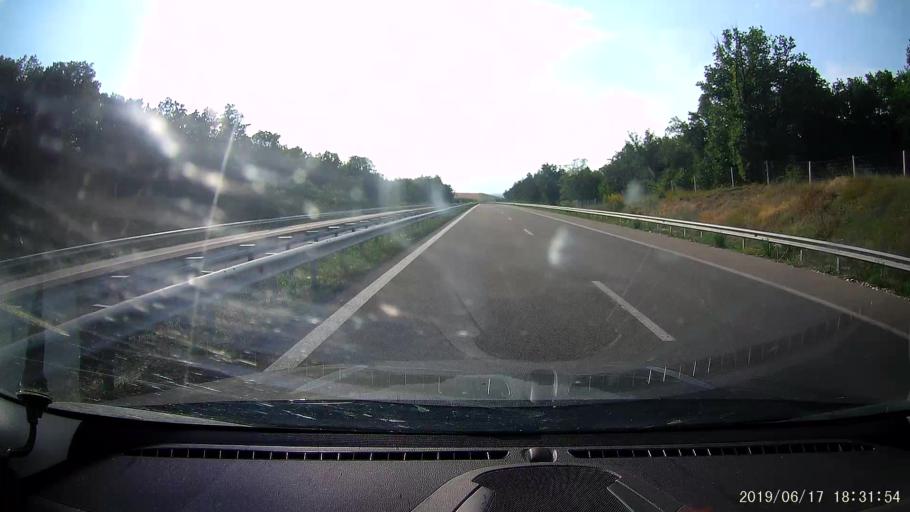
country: BG
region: Khaskovo
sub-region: Obshtina Dimitrovgrad
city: Dimitrovgrad
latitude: 42.0522
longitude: 25.4923
